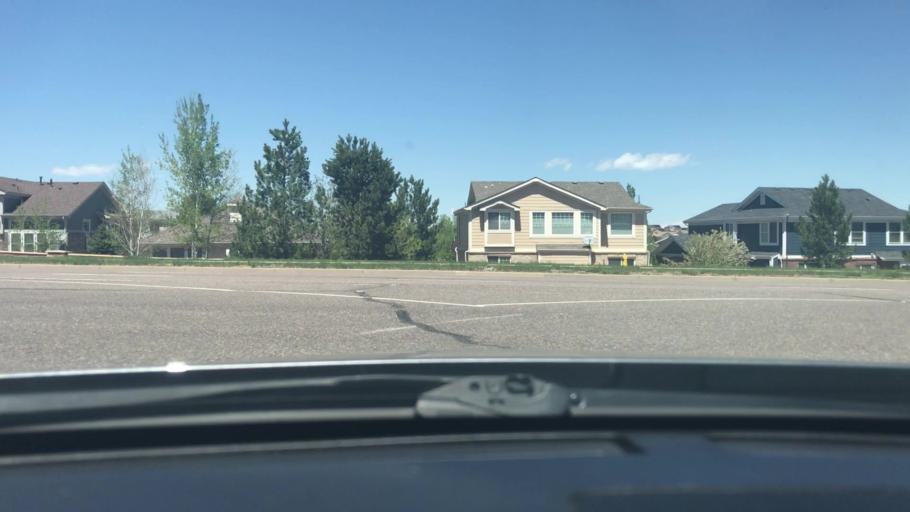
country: US
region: Colorado
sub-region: Arapahoe County
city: Dove Valley
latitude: 39.6529
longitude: -104.7438
